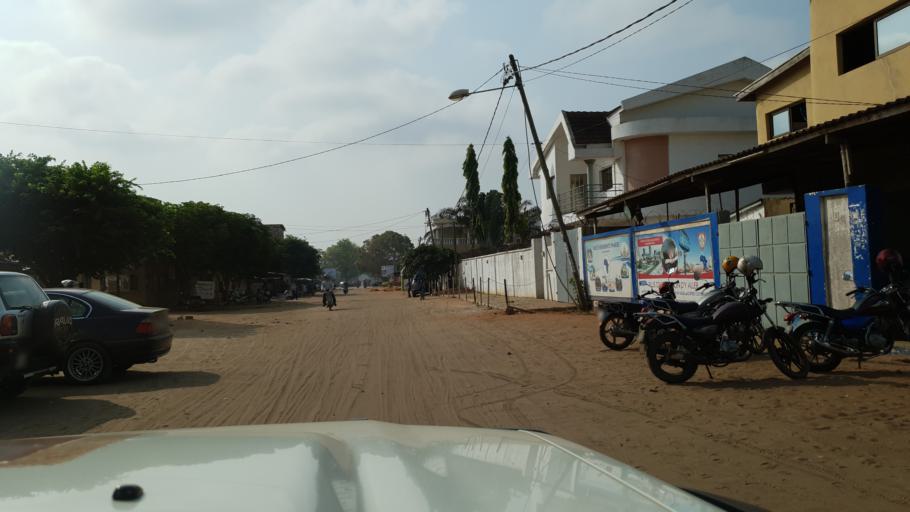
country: TG
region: Maritime
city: Lome
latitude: 6.1647
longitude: 1.2142
